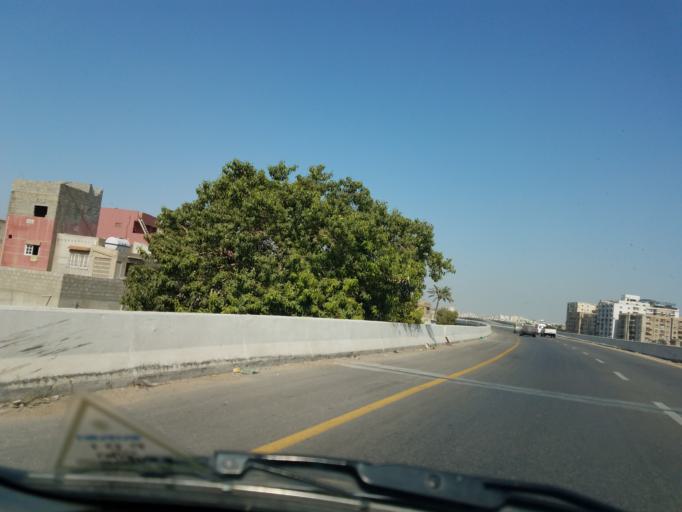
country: PK
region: Sindh
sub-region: Karachi District
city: Karachi
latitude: 24.8804
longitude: 67.0163
